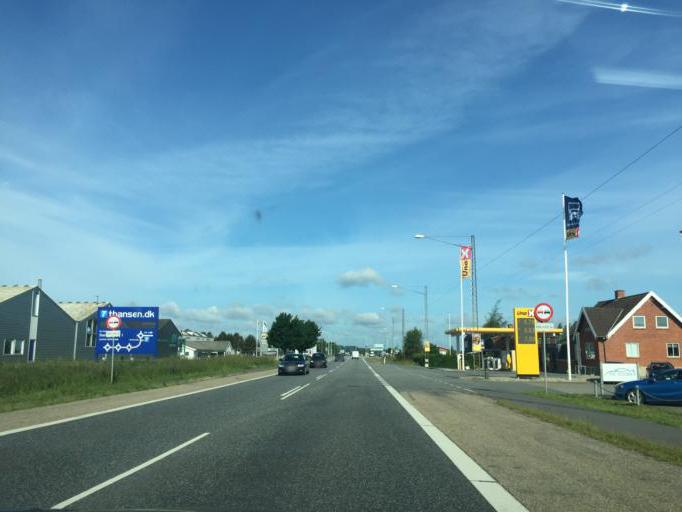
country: DK
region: South Denmark
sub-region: Middelfart Kommune
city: Middelfart
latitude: 55.4963
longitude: 9.7716
